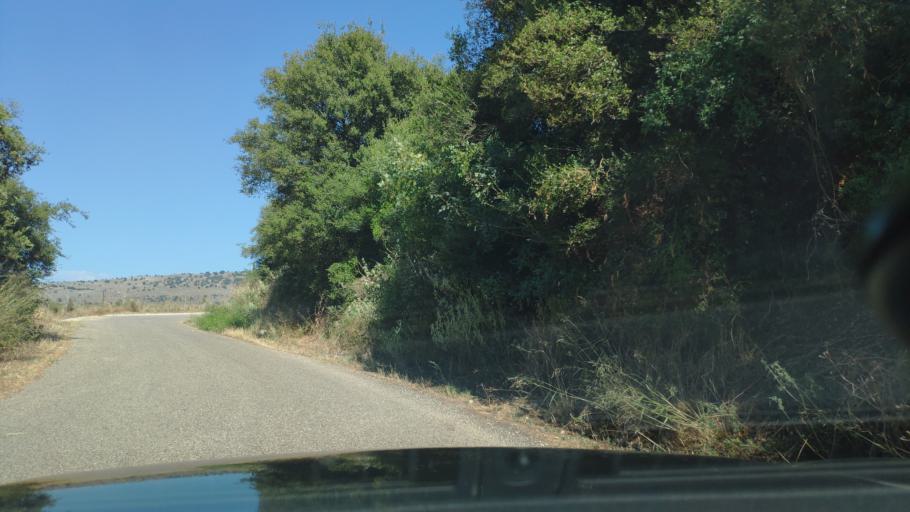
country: GR
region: West Greece
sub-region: Nomos Aitolias kai Akarnanias
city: Katouna
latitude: 38.8166
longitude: 21.1046
